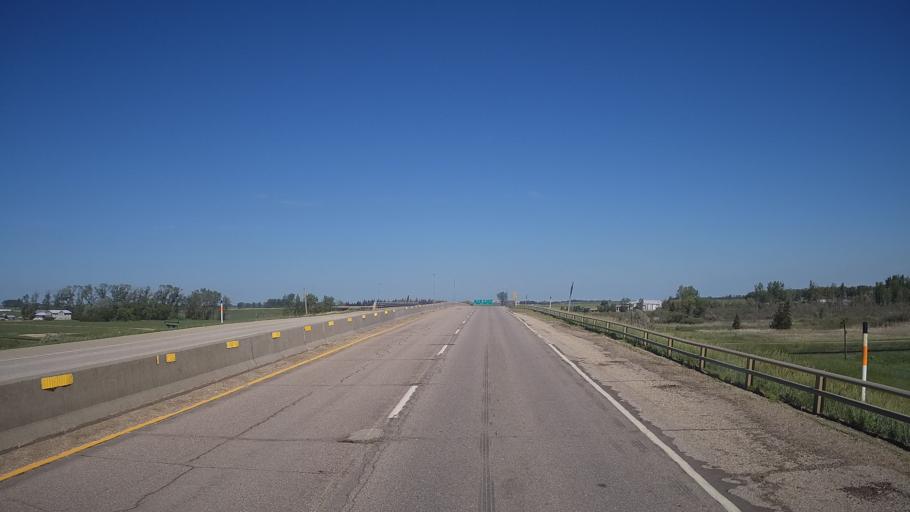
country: CA
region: Manitoba
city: Portage la Prairie
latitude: 49.9666
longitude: -98.3564
